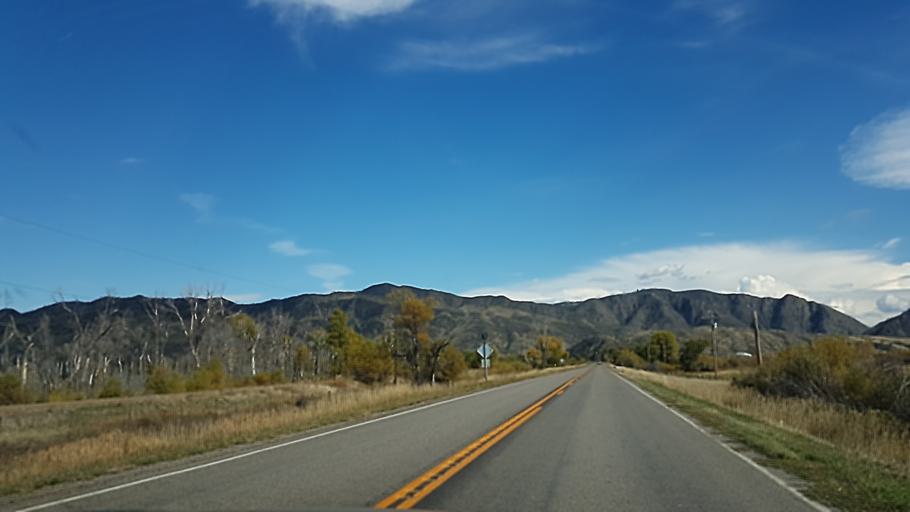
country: US
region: Montana
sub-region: Jefferson County
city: Whitehall
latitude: 45.8526
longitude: -111.9489
